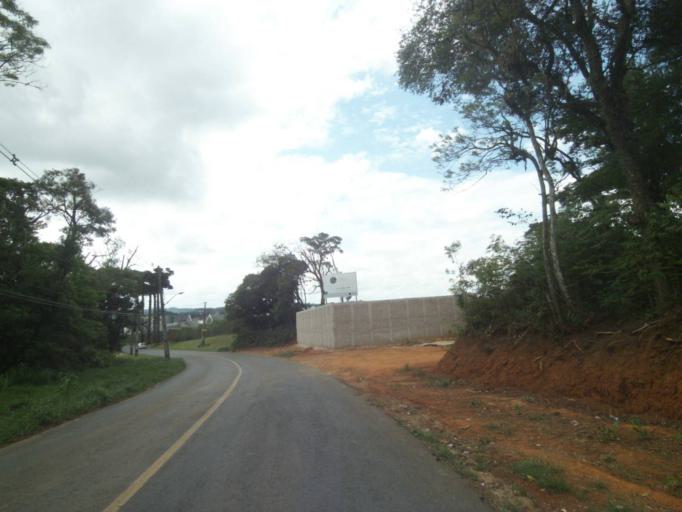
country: BR
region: Parana
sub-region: Curitiba
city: Curitiba
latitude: -25.3825
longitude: -49.2881
